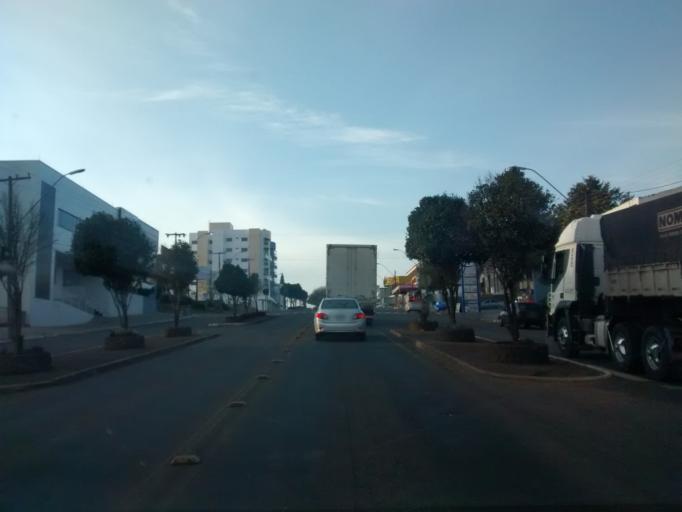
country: BR
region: Parana
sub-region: Francisco Beltrao
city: Francisco Beltrao
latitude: -26.1448
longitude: -53.0270
